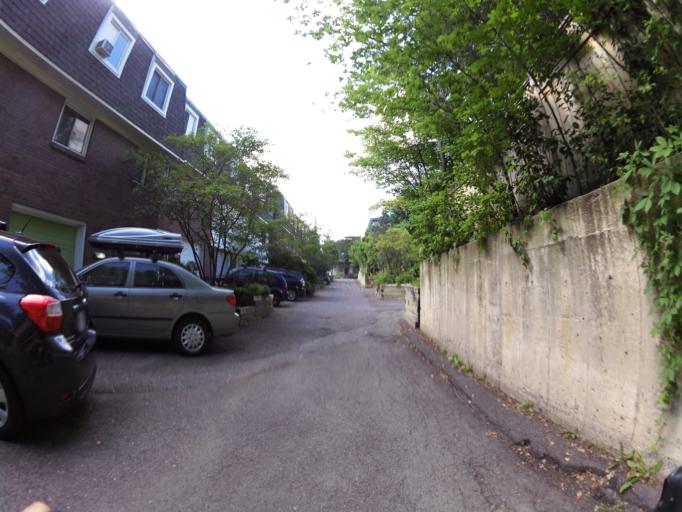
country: CA
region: Ontario
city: Ottawa
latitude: 45.3899
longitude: -75.6824
